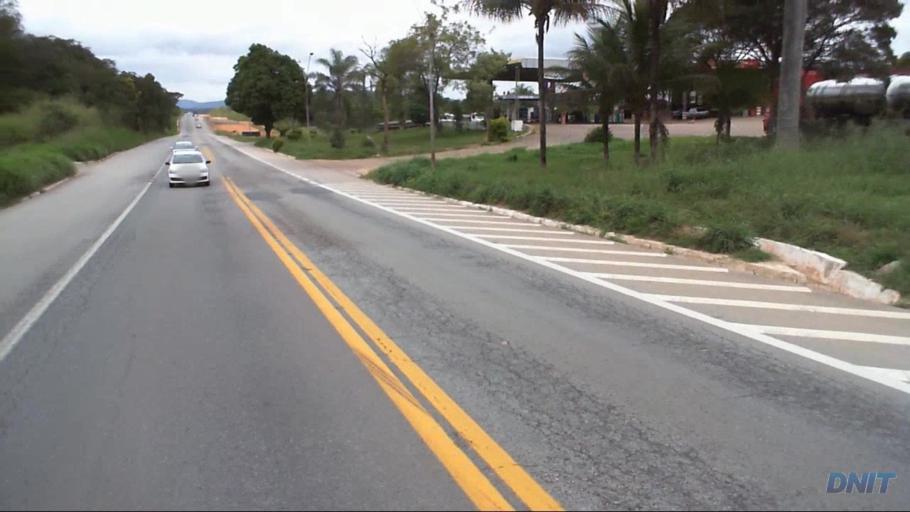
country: BR
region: Minas Gerais
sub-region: Barao De Cocais
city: Barao de Cocais
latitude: -19.7724
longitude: -43.4465
